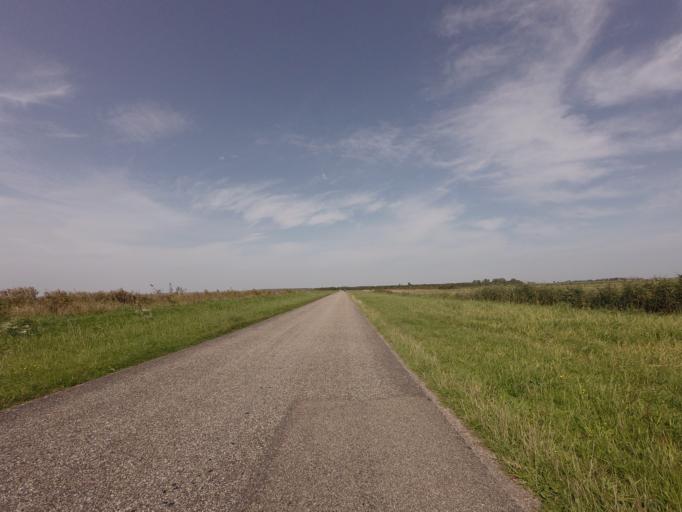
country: NL
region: Groningen
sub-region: Gemeente De Marne
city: Ulrum
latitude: 53.3502
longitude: 6.2664
